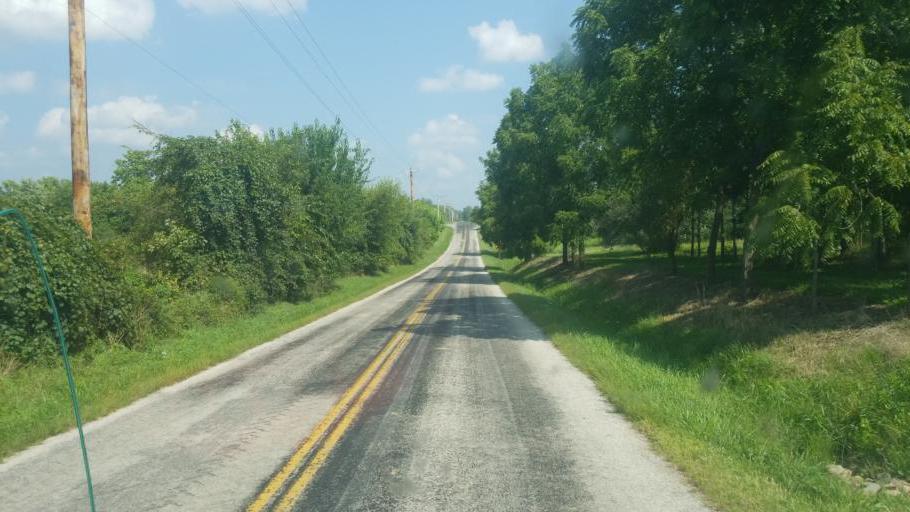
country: US
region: Ohio
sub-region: Lorain County
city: Wellington
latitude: 41.0576
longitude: -82.2614
